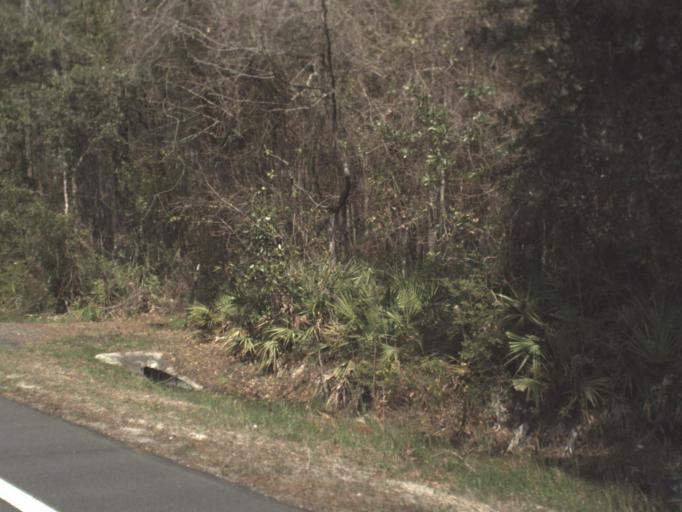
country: US
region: Florida
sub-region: Wakulla County
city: Crawfordville
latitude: 30.0035
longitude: -84.5038
